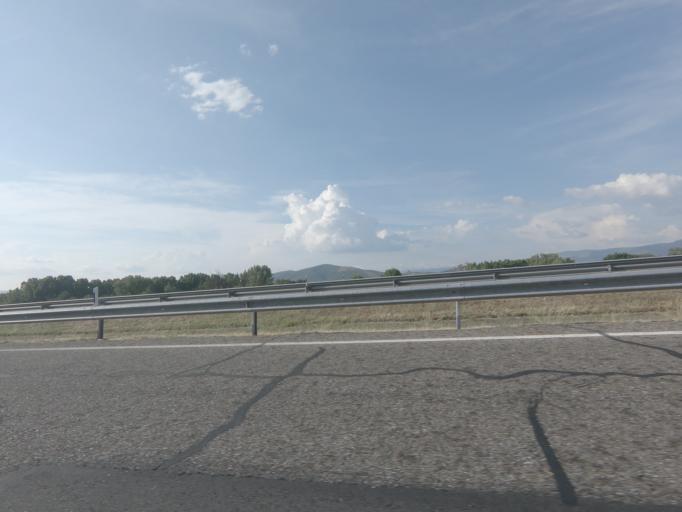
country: ES
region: Galicia
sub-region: Provincia de Ourense
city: Verin
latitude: 41.9220
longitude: -7.4631
